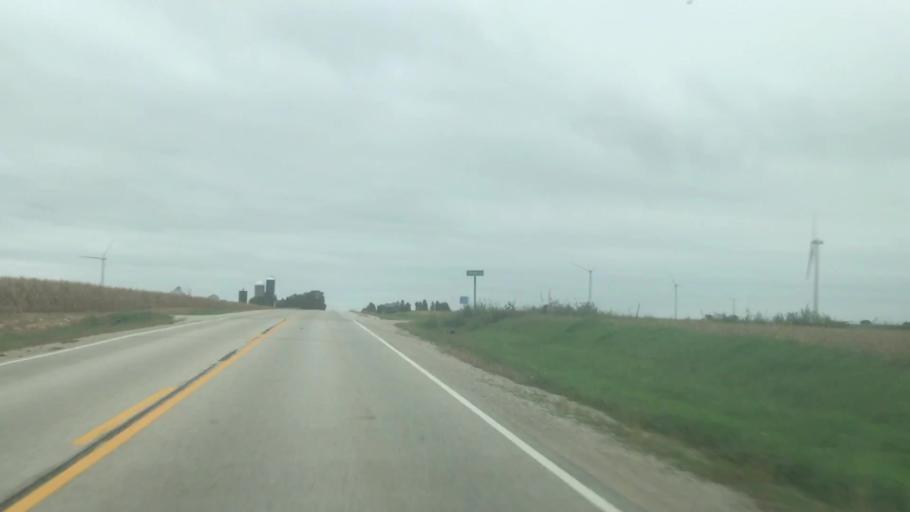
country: US
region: Wisconsin
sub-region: Fond du Lac County
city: Oakfield
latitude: 43.6324
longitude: -88.5418
